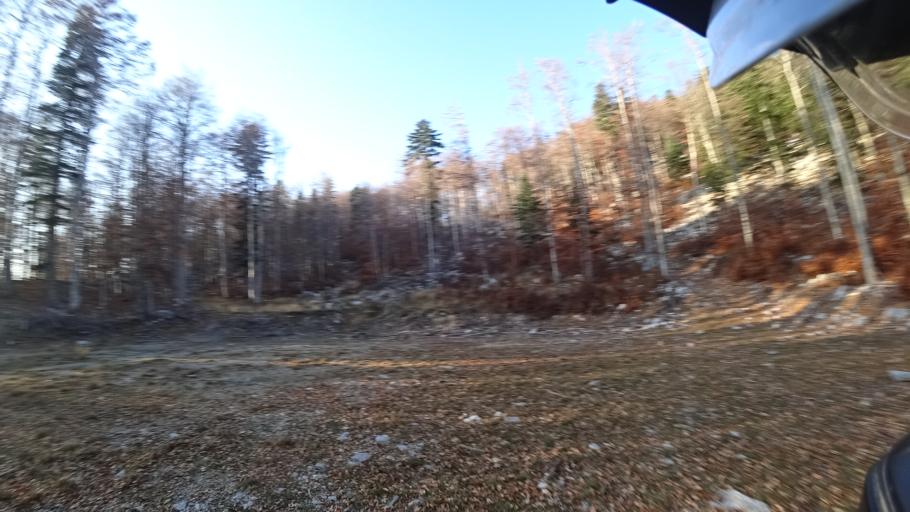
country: HR
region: Primorsko-Goranska
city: Drazice
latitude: 45.4815
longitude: 14.4931
